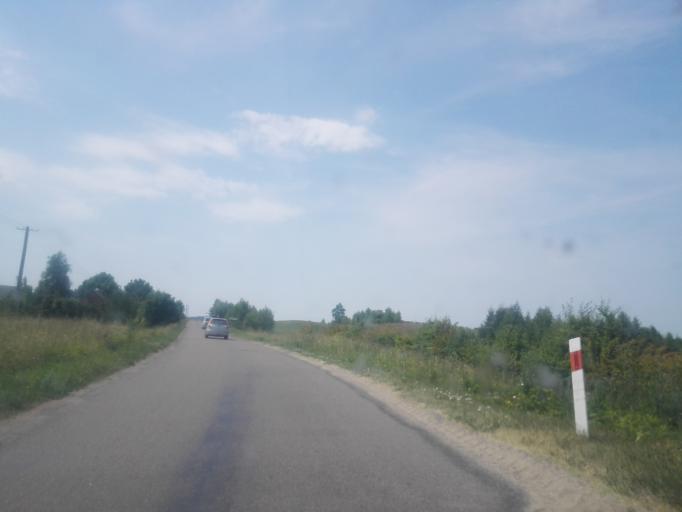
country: PL
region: Podlasie
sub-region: Powiat sejnenski
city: Krasnopol
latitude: 54.0533
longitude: 23.1411
